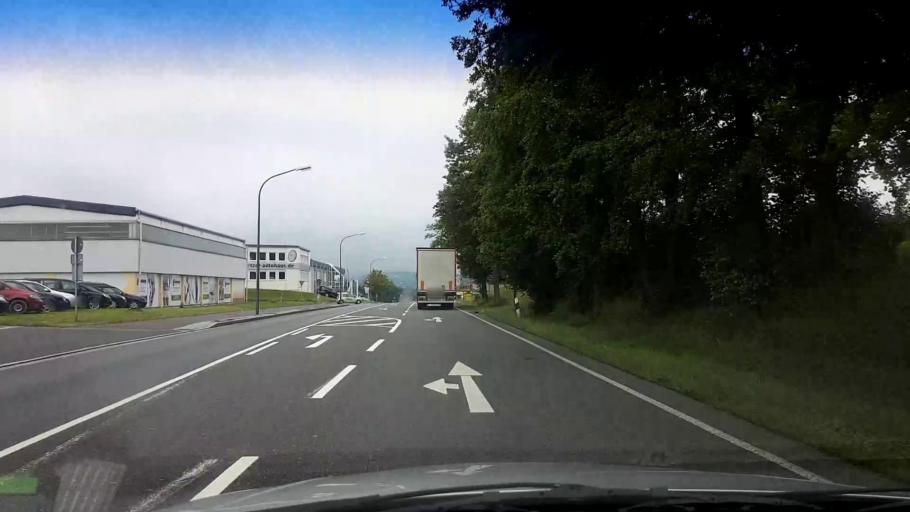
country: DE
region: Bavaria
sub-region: Upper Franconia
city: Marktredwitz
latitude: 50.0094
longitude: 12.0776
